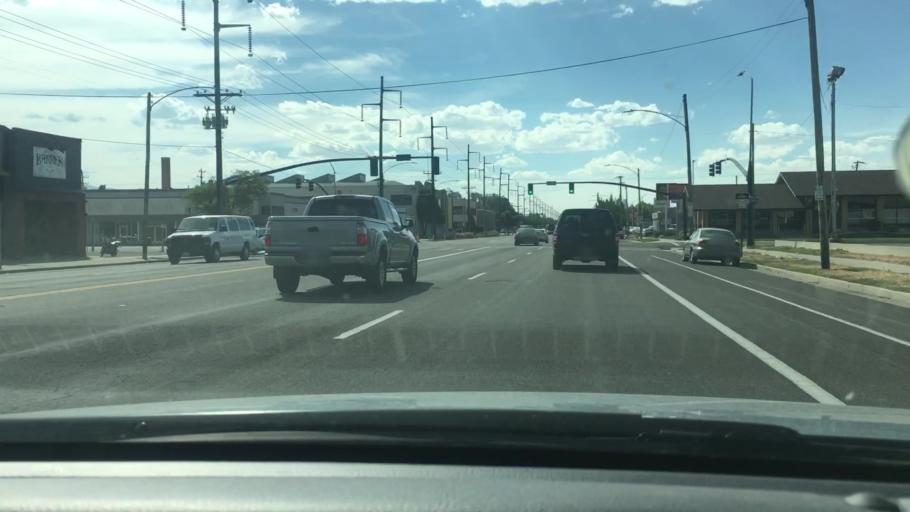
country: US
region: Utah
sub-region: Salt Lake County
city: Salt Lake City
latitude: 40.7520
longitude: -111.8902
